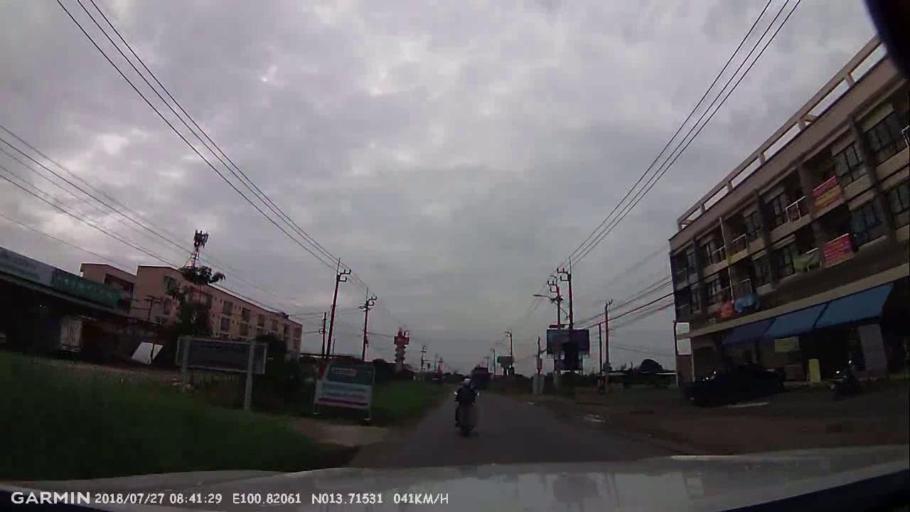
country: TH
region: Bangkok
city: Lat Krabang
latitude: 13.7151
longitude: 100.8202
